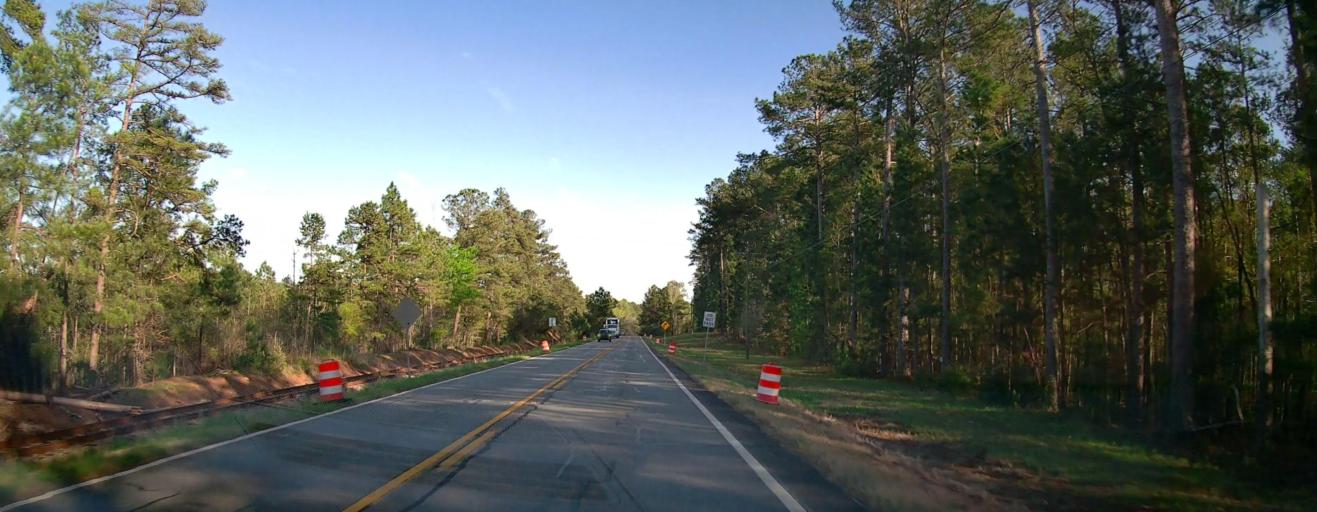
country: US
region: Georgia
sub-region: Baldwin County
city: Milledgeville
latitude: 33.1244
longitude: -83.2961
